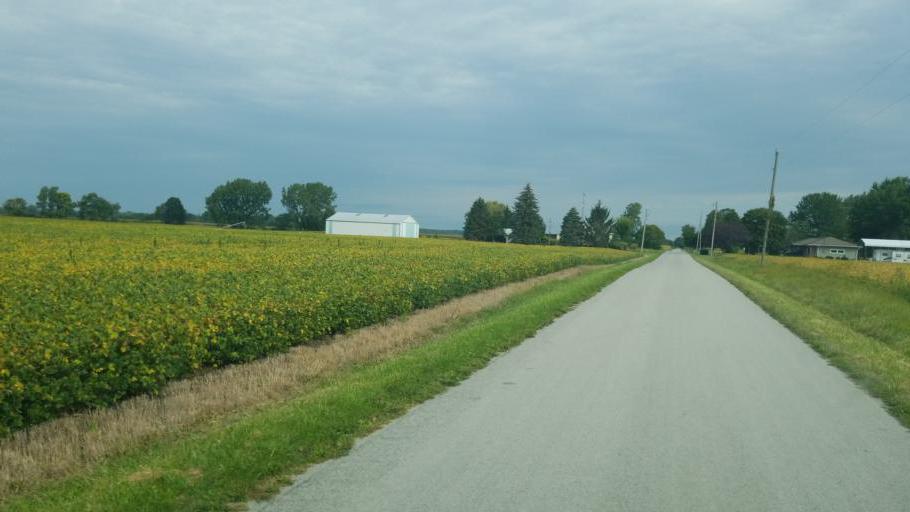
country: US
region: Ohio
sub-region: Wyandot County
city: Upper Sandusky
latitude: 40.7495
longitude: -83.1690
